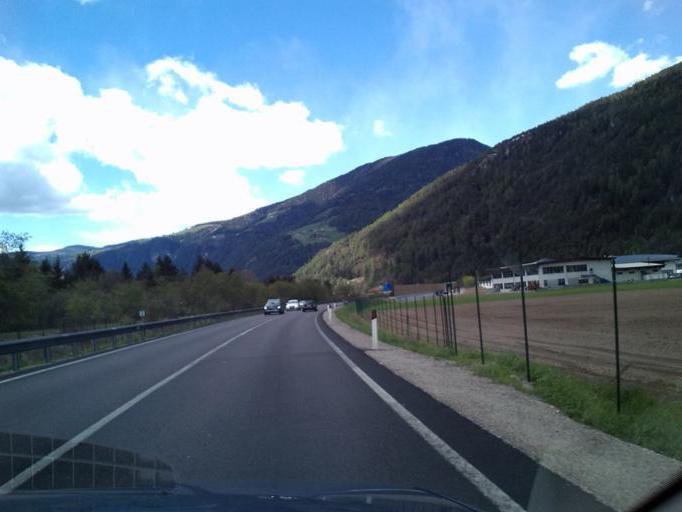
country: IT
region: Trentino-Alto Adige
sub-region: Bolzano
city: Vandoies di Sotto
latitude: 46.8109
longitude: 11.7459
